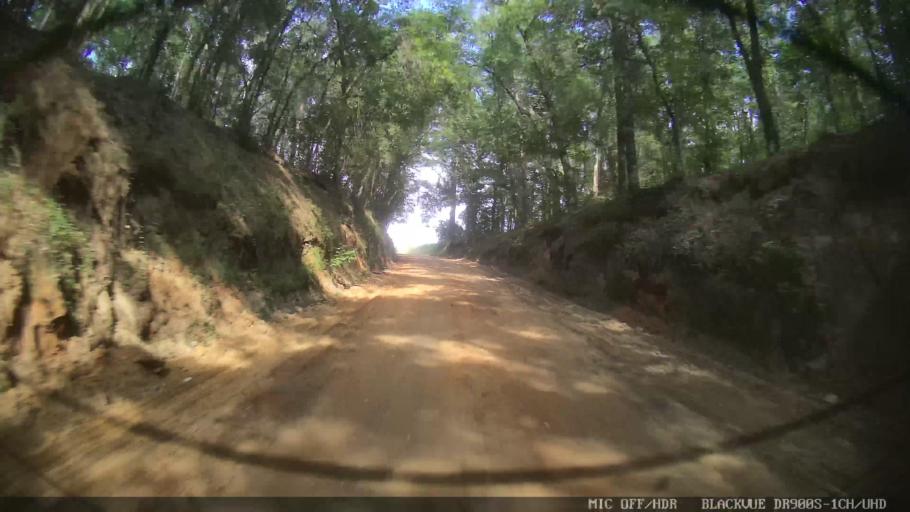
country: US
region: Georgia
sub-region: Lowndes County
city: Valdosta
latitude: 30.6181
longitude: -83.2328
